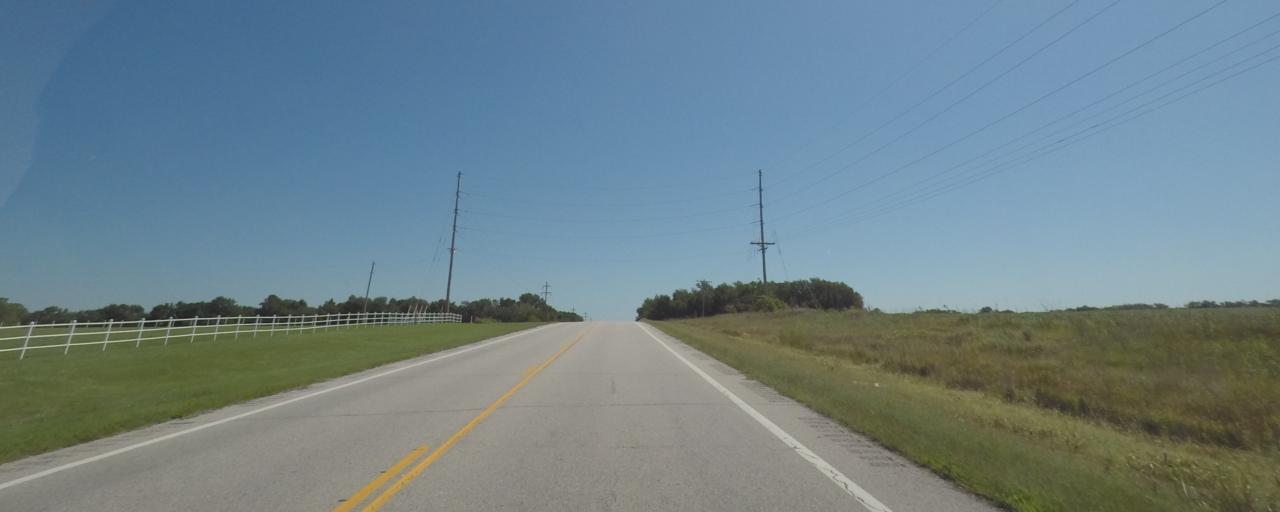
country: US
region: Kansas
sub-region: Sumner County
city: Belle Plaine
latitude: 37.3912
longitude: -97.3751
